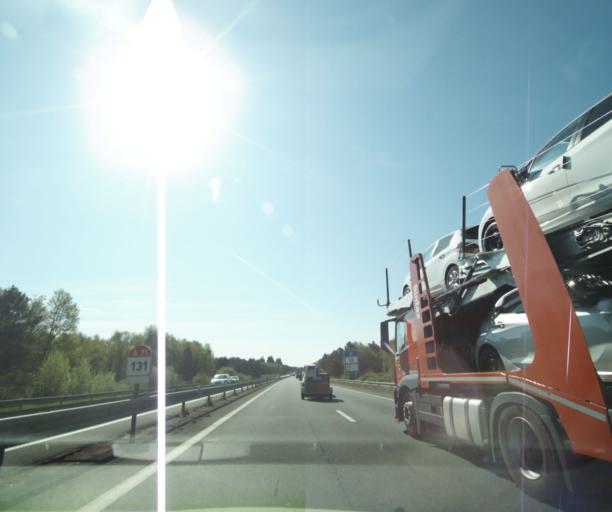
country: FR
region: Centre
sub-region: Departement du Loir-et-Cher
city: Chaumont-sur-Tharonne
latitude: 47.6366
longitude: 1.9510
